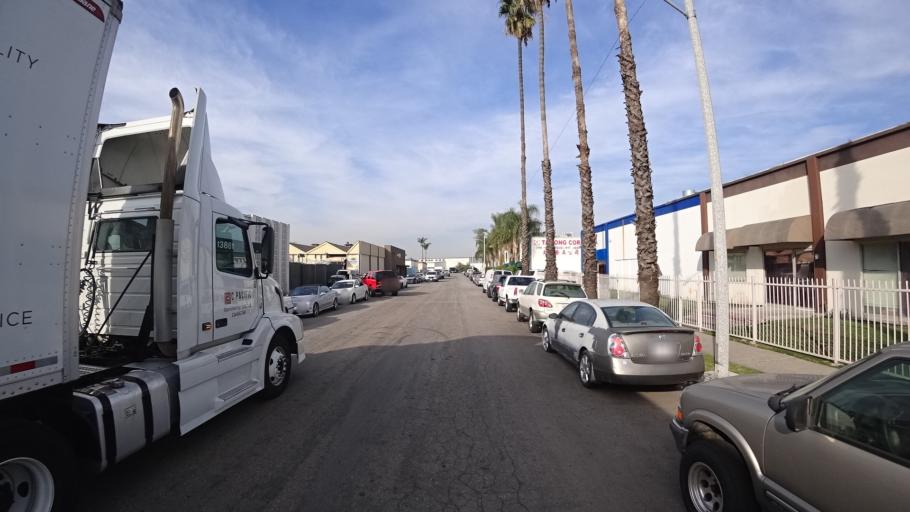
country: US
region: California
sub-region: Orange County
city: Garden Grove
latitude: 33.7609
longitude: -117.9238
